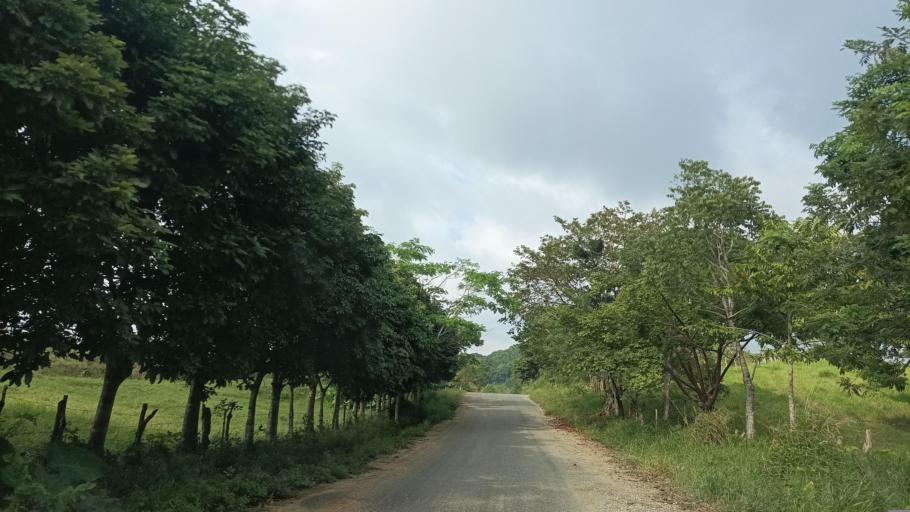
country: MX
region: Veracruz
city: Allende
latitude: 18.1146
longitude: -94.2915
